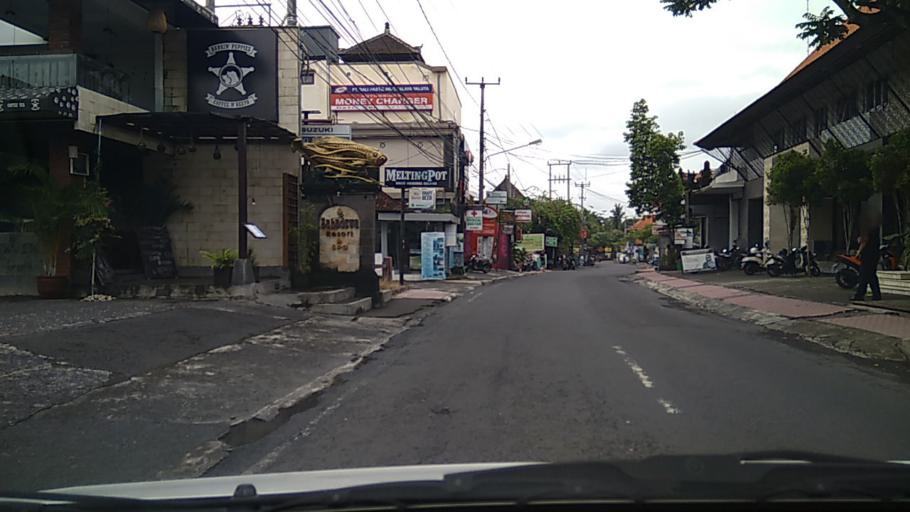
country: ID
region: Bali
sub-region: Kabupaten Gianyar
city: Ubud
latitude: -8.5192
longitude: 115.2633
